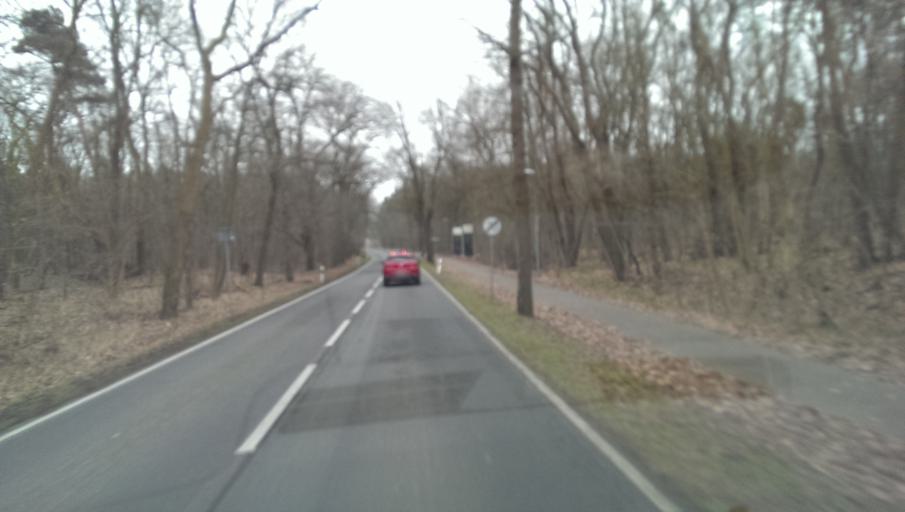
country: DE
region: Brandenburg
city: Grossbeeren
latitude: 52.3207
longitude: 13.3061
